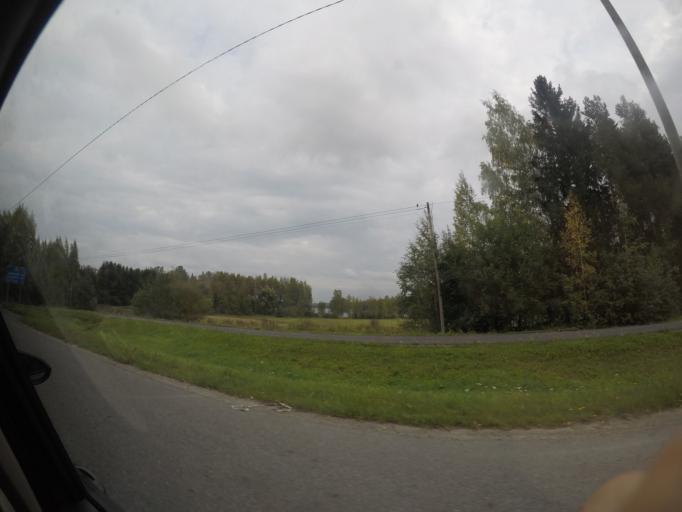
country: FI
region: Haeme
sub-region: Haemeenlinna
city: Haemeenlinna
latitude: 61.0254
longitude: 24.4219
